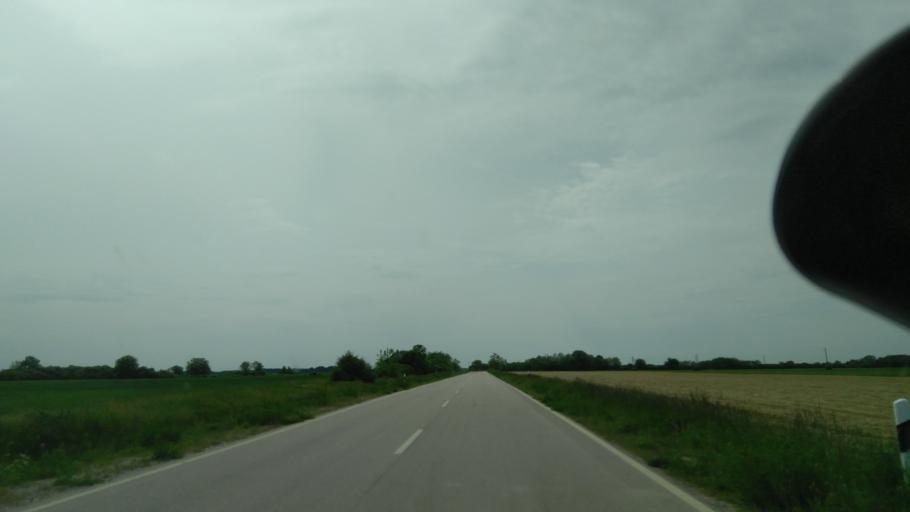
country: HU
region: Bekes
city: Mehkerek
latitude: 46.8674
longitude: 21.5007
